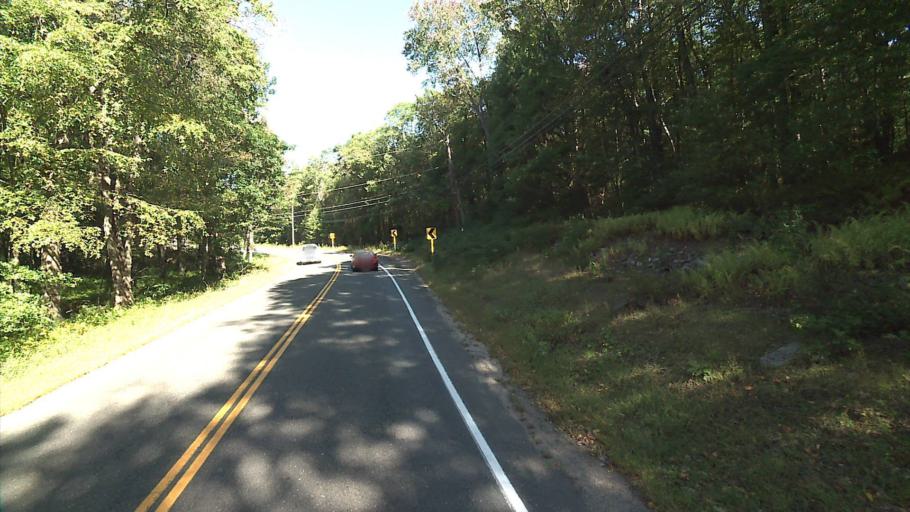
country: US
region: Connecticut
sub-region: Hartford County
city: Bristol
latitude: 41.7323
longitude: -72.9531
